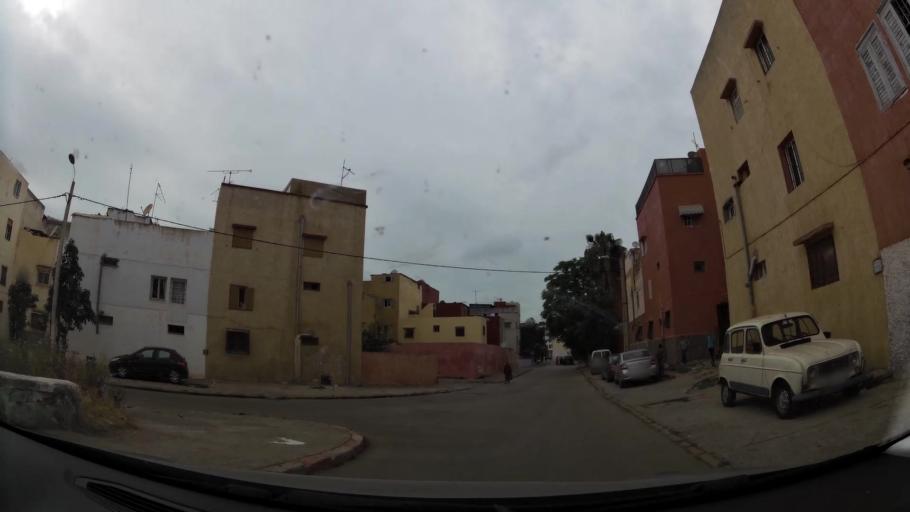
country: MA
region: Rabat-Sale-Zemmour-Zaer
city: Sale
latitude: 34.0477
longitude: -6.7986
